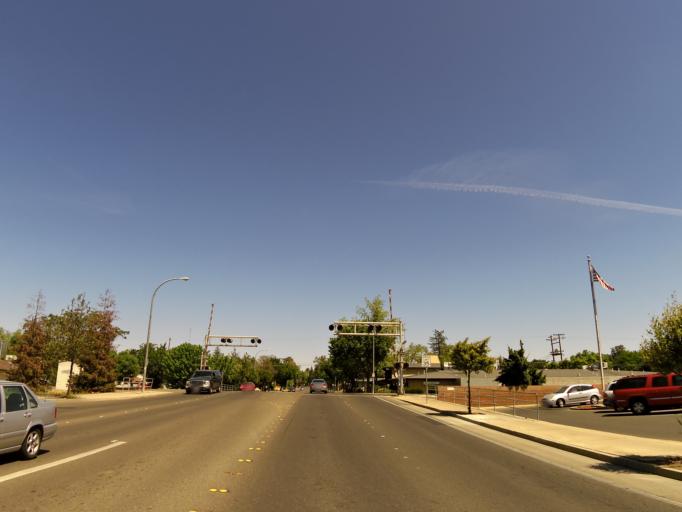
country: US
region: California
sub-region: Merced County
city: Merced
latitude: 37.3084
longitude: -120.4809
